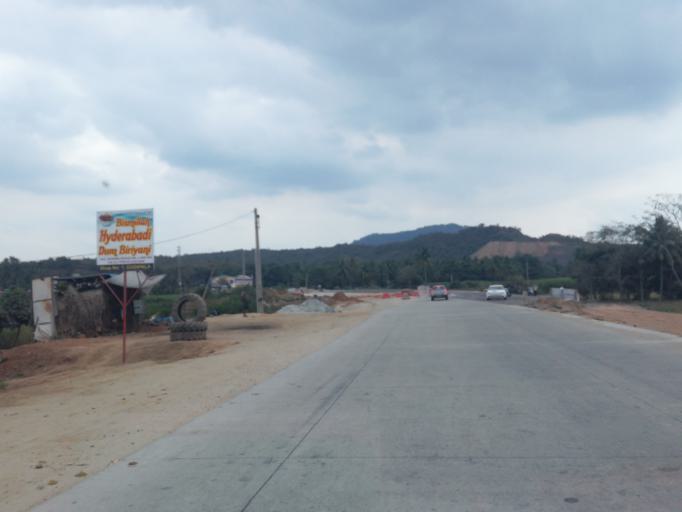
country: IN
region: Andhra Pradesh
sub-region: Chittoor
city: Ramapuram
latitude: 13.0988
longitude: 79.1253
